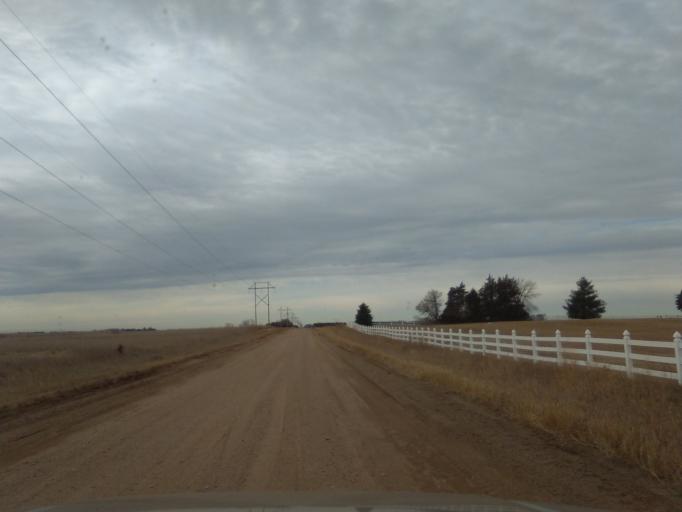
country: US
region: Nebraska
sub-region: Buffalo County
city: Gibbon
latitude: 40.6549
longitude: -98.7625
